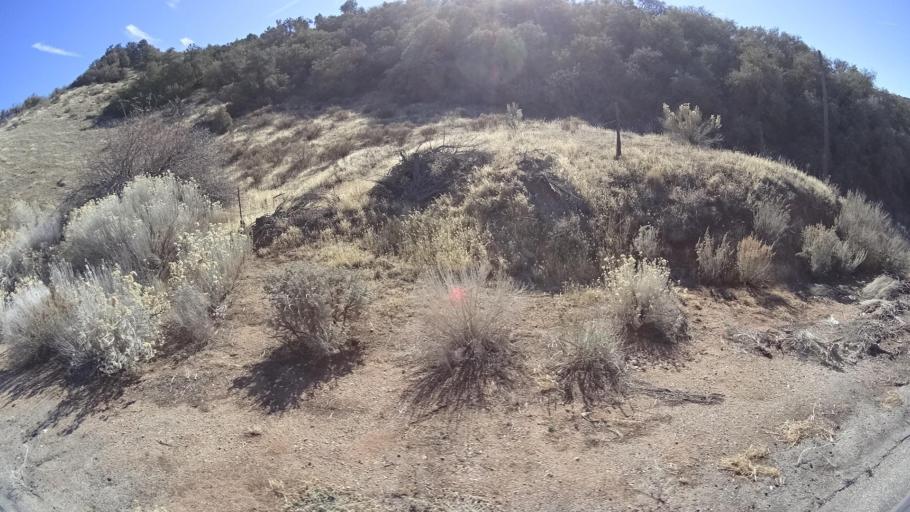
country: US
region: California
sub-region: Kern County
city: Maricopa
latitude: 34.8803
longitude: -119.3531
